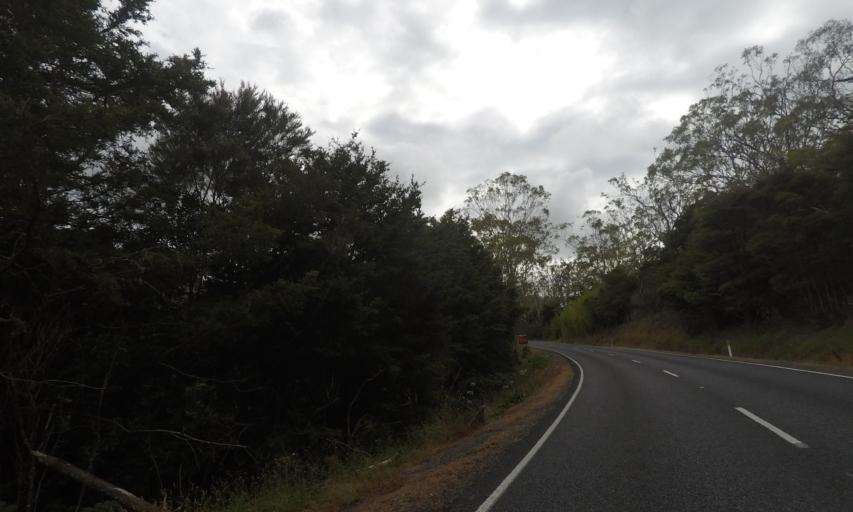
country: NZ
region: Northland
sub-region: Whangarei
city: Ruakaka
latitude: -35.7650
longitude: 174.4671
